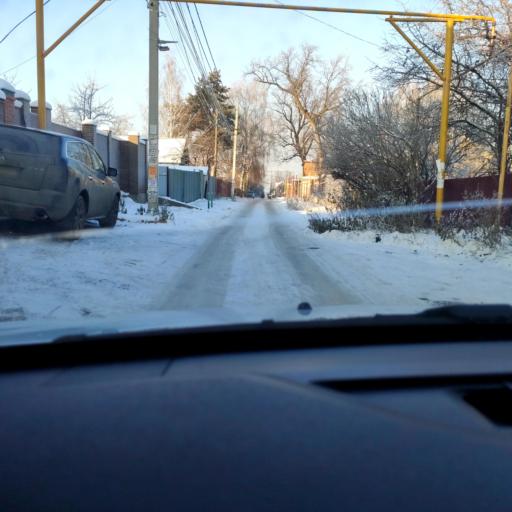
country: RU
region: Samara
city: Samara
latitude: 53.2725
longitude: 50.2024
